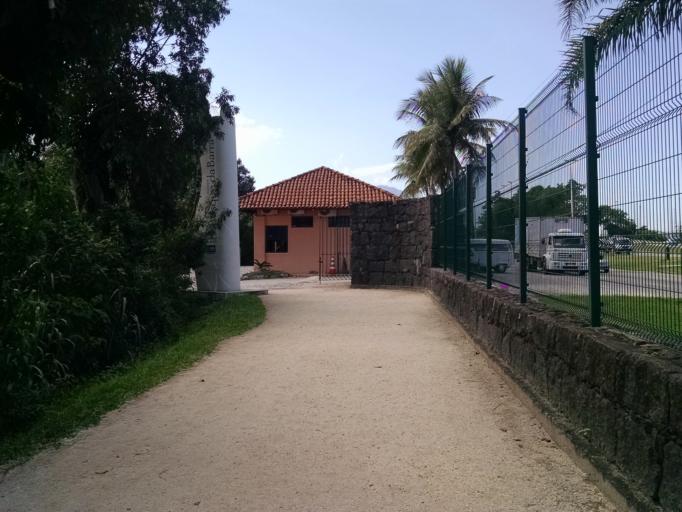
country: BR
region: Rio de Janeiro
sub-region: Rio De Janeiro
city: Rio de Janeiro
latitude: -22.9998
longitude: -43.3721
